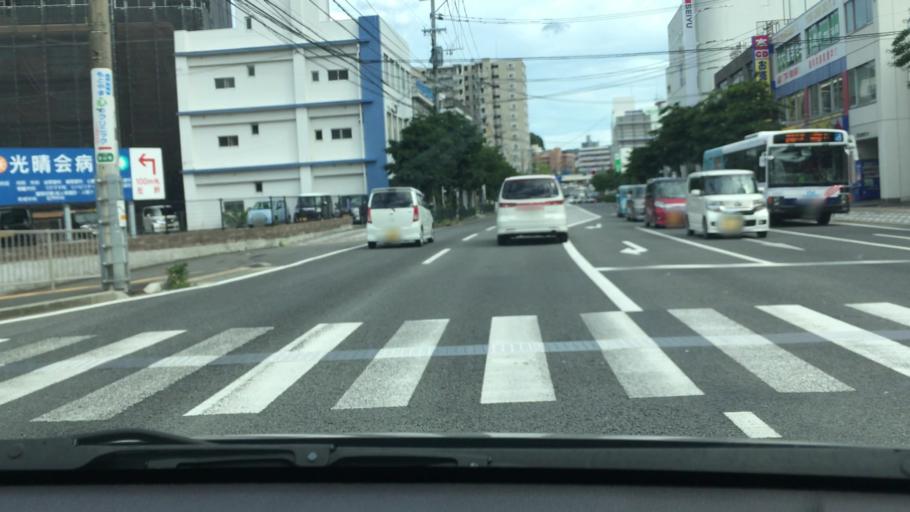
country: JP
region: Nagasaki
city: Togitsu
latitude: 32.8049
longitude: 129.8506
